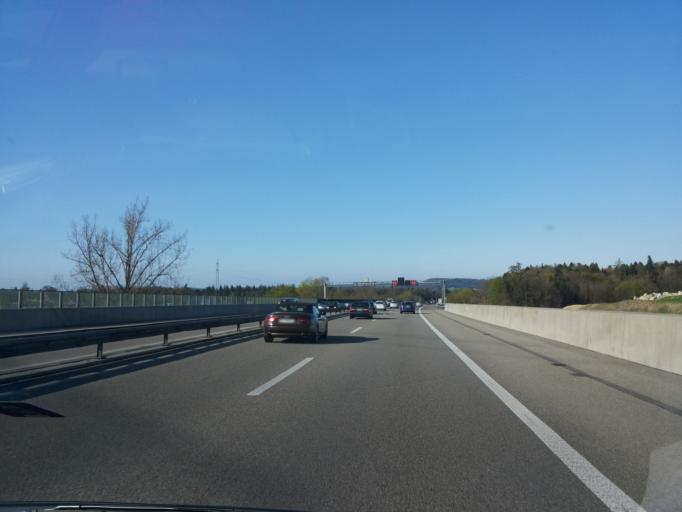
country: CH
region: Aargau
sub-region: Bezirk Lenzburg
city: Othmarsingen
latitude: 47.4165
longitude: 8.2228
